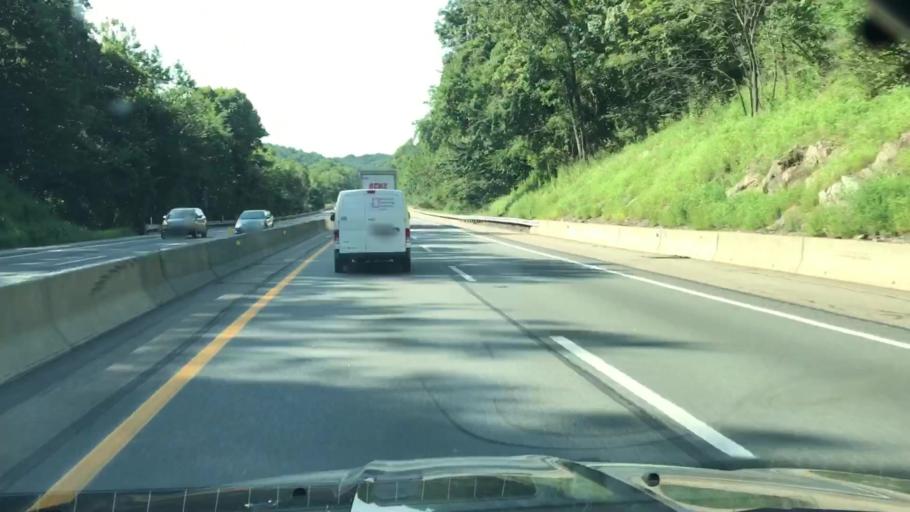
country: US
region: Pennsylvania
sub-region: Chester County
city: Downingtown
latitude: 40.0878
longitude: -75.7257
